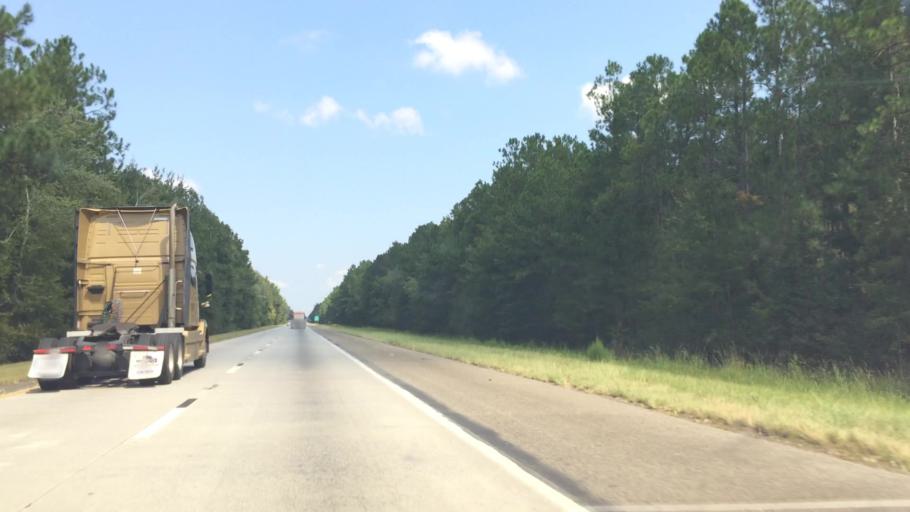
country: US
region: South Carolina
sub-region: Dorchester County
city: Saint George
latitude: 33.0613
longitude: -80.6629
